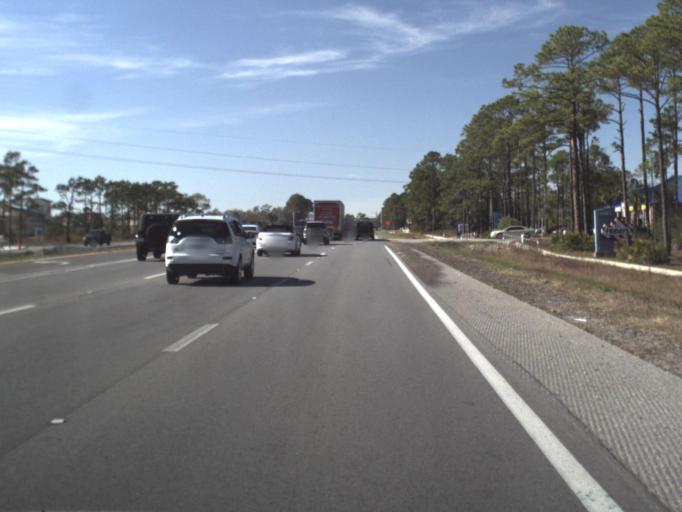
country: US
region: Florida
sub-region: Bay County
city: Panama City Beach
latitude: 30.1982
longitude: -85.8156
